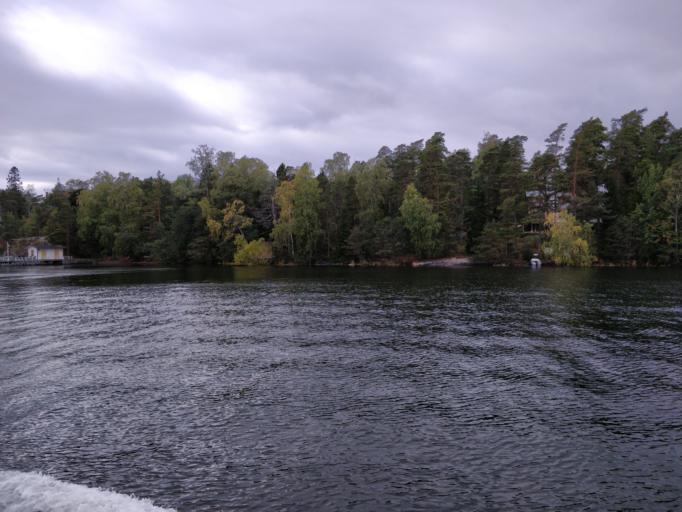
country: FI
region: Uusimaa
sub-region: Helsinki
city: Vantaa
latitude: 60.1635
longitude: 25.0991
